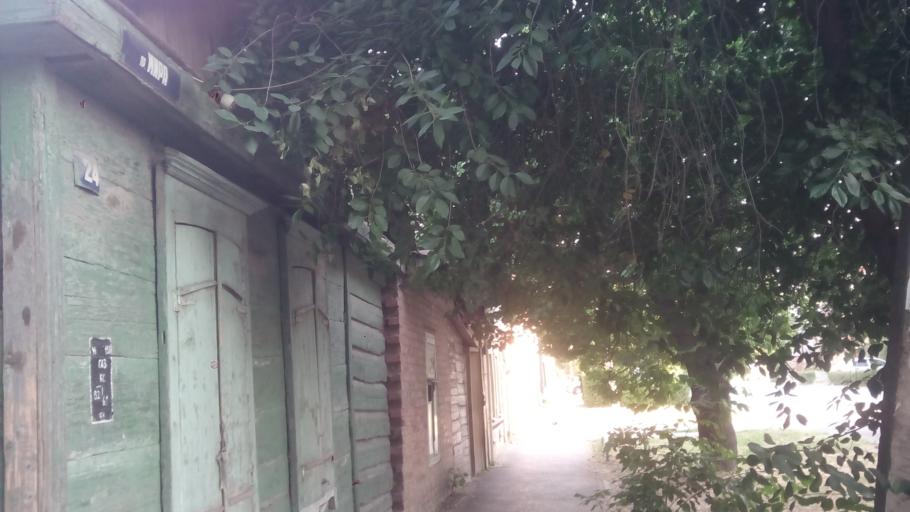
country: RU
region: Rostov
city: Imeni Chkalova
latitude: 47.2480
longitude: 39.7691
